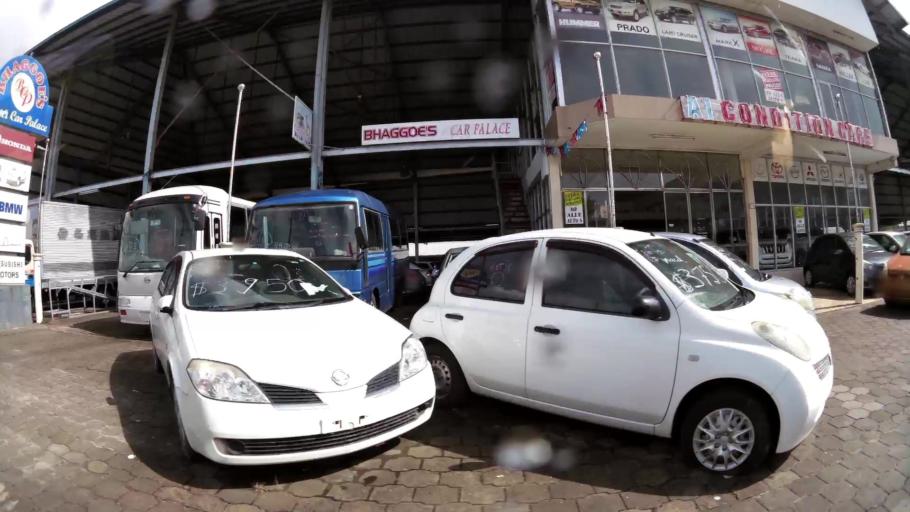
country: SR
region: Paramaribo
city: Paramaribo
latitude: 5.8423
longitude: -55.2045
